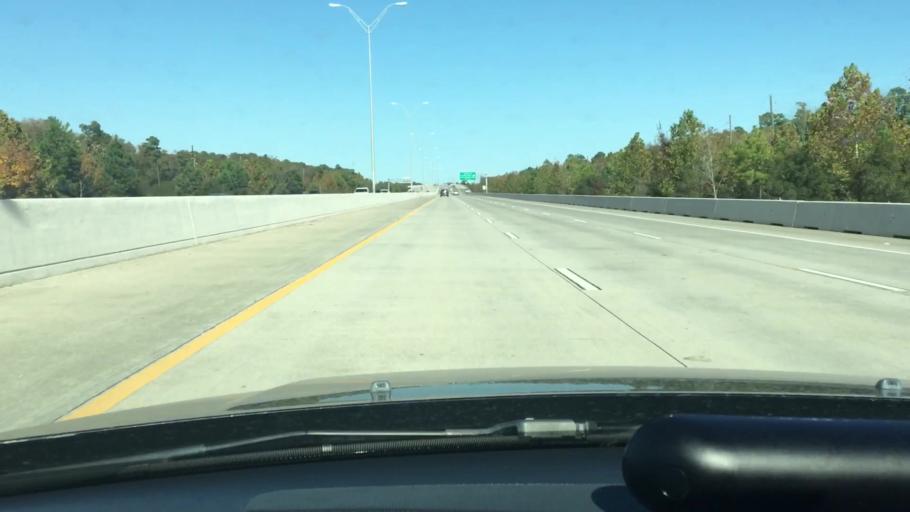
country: US
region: Texas
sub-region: Harris County
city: Sheldon
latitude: 29.8623
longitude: -95.1871
